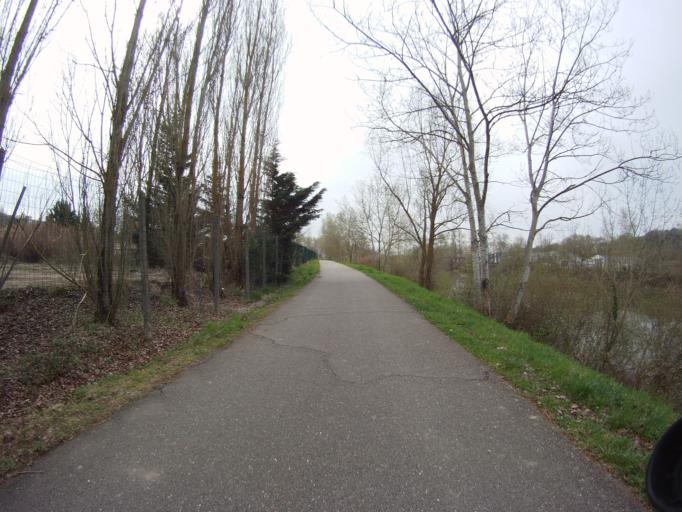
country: FR
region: Lorraine
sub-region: Departement de Meurthe-et-Moselle
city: Malzeville
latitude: 48.7242
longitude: 6.1754
